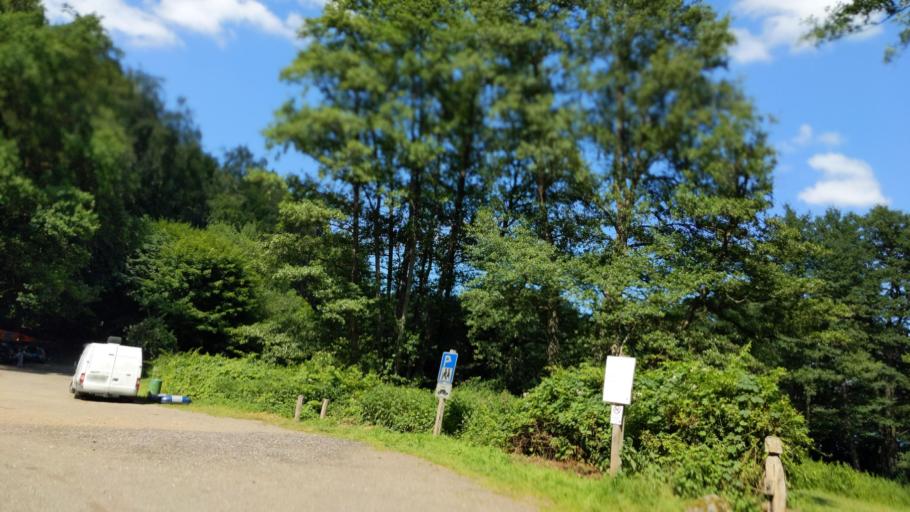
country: DE
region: Schleswig-Holstein
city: Schmilau
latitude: 53.6814
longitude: 10.7526
